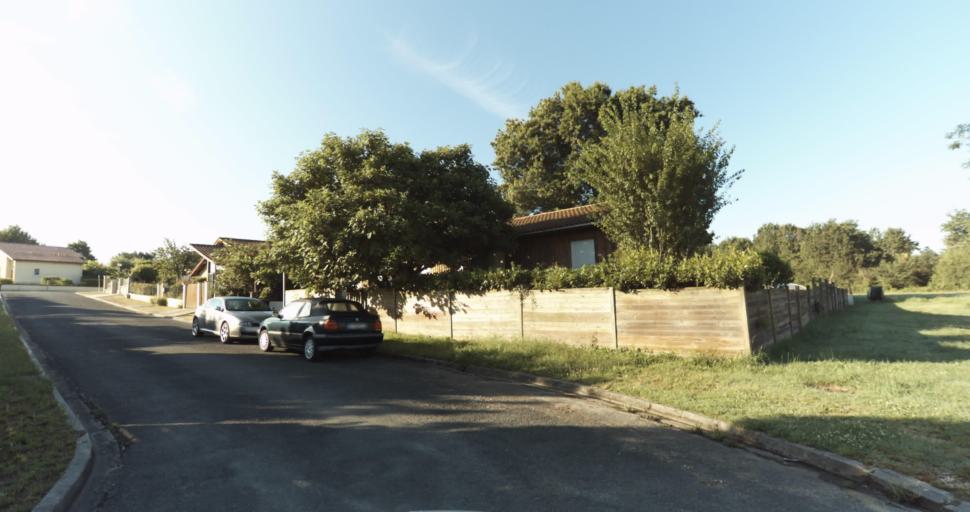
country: FR
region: Aquitaine
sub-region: Departement de la Gironde
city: Bazas
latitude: 44.4247
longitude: -0.2202
